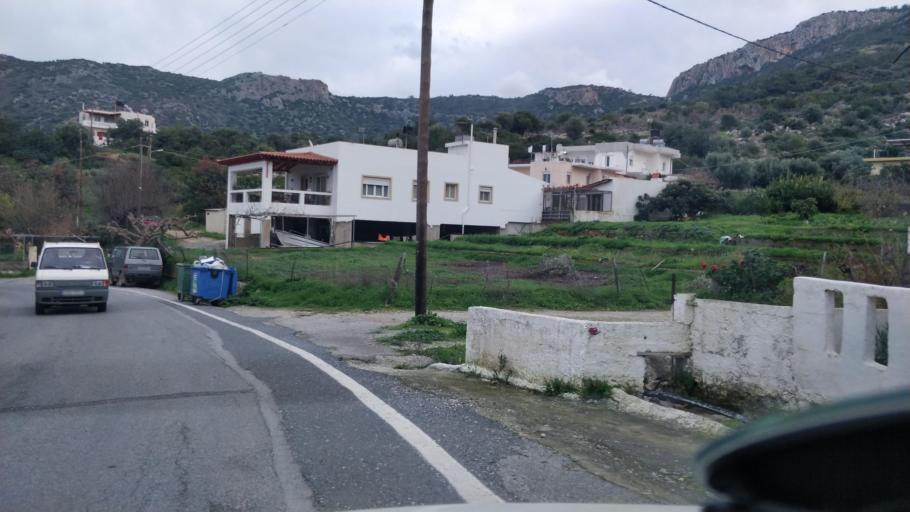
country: GR
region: Crete
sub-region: Nomos Lasithiou
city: Agios Nikolaos
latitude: 35.1148
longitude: 25.7255
